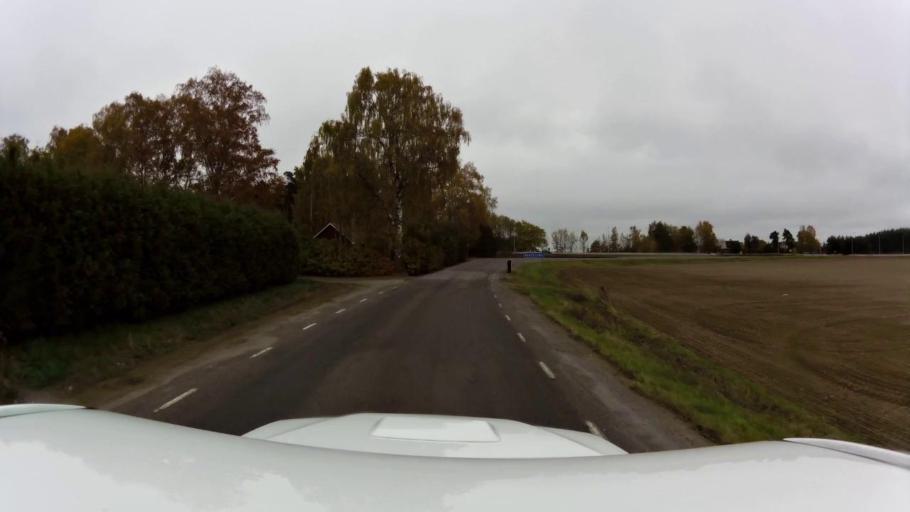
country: SE
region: OEstergoetland
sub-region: Linkopings Kommun
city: Linghem
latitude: 58.4318
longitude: 15.7203
